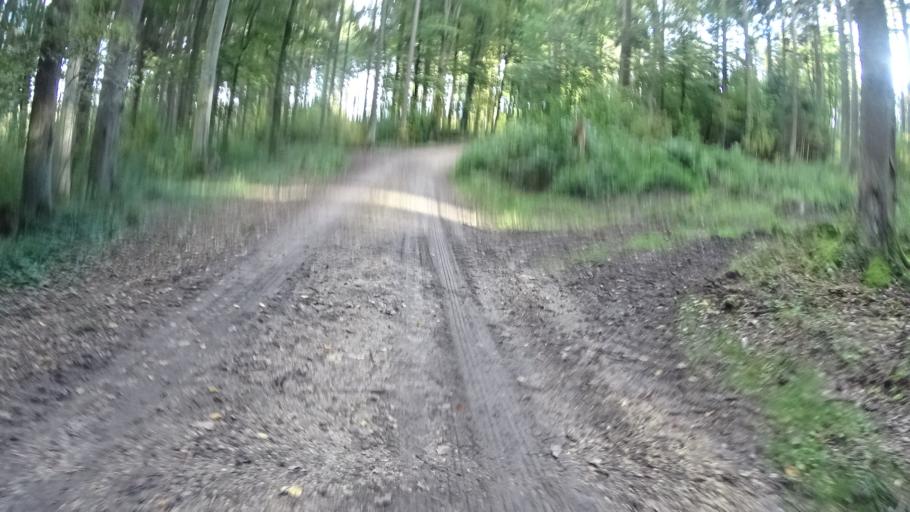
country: DE
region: Bavaria
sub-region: Upper Bavaria
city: Bohmfeld
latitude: 48.8761
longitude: 11.3579
